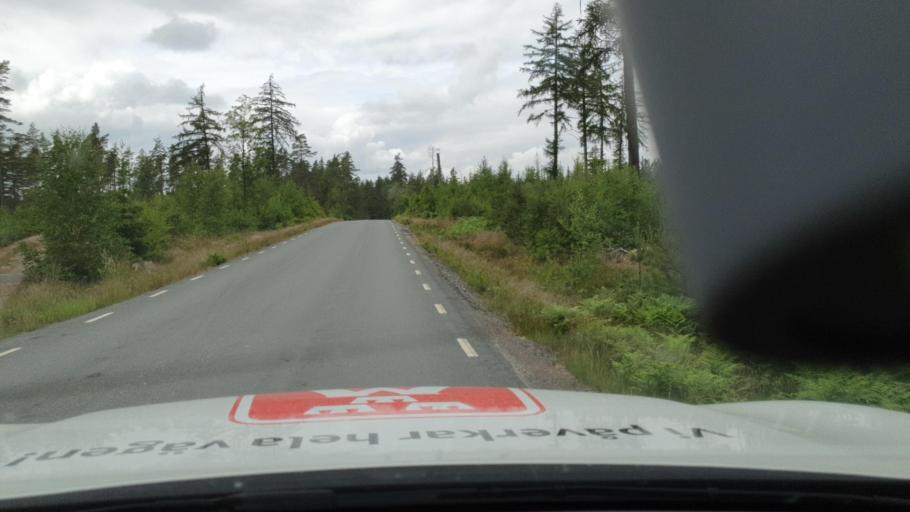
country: SE
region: Vaestra Goetaland
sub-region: Tidaholms Kommun
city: Tidaholm
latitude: 58.1004
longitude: 14.0886
